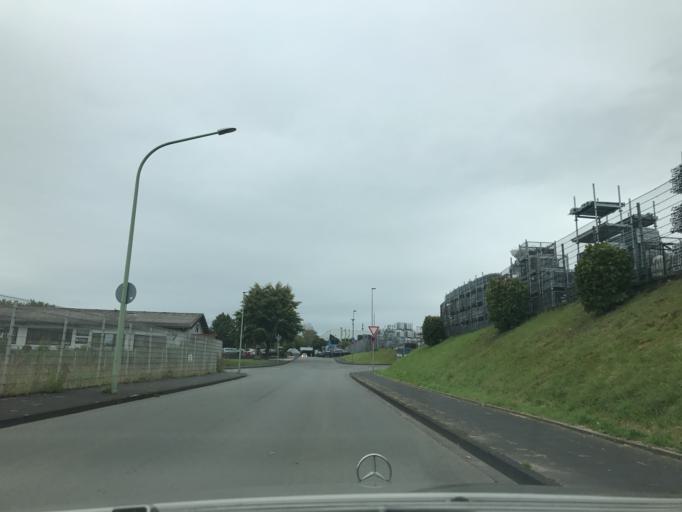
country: DE
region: North Rhine-Westphalia
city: Wetter (Ruhr)
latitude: 51.3388
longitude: 7.4025
